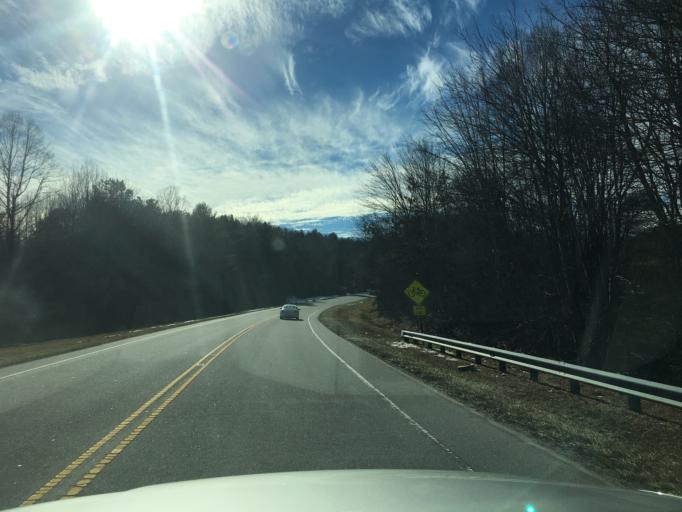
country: US
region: North Carolina
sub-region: Transylvania County
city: Brevard
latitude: 35.1850
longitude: -82.7922
